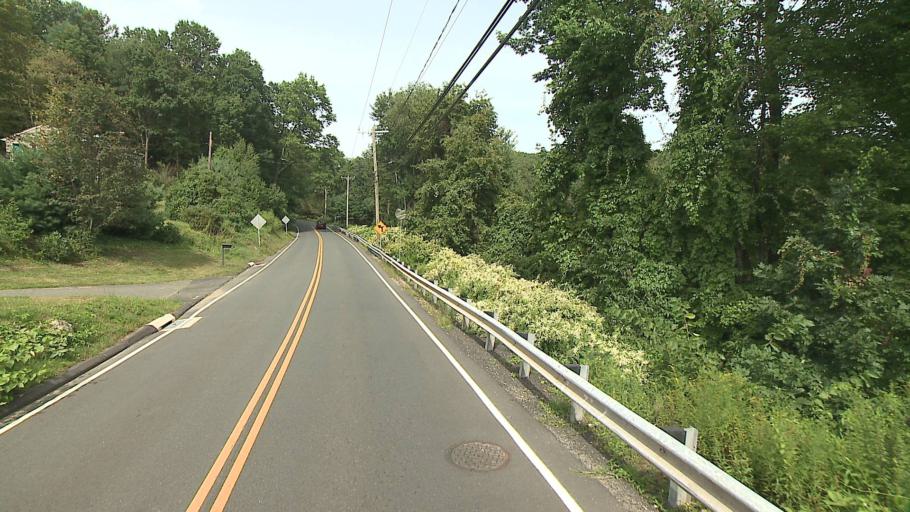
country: US
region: Connecticut
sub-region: Litchfield County
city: Plymouth
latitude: 41.6611
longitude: -73.0486
